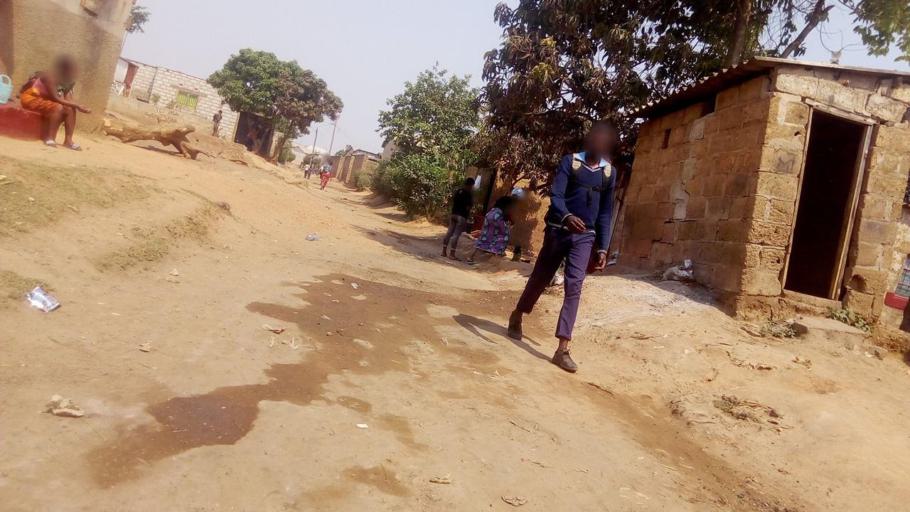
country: ZM
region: Lusaka
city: Lusaka
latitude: -15.3580
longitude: 28.2947
